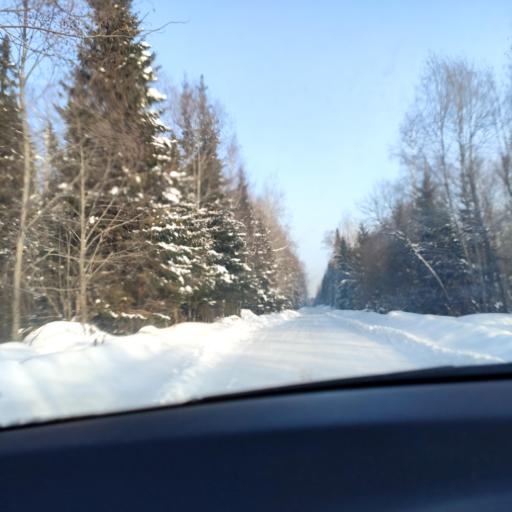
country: RU
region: Perm
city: Kondratovo
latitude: 58.0758
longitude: 56.1294
